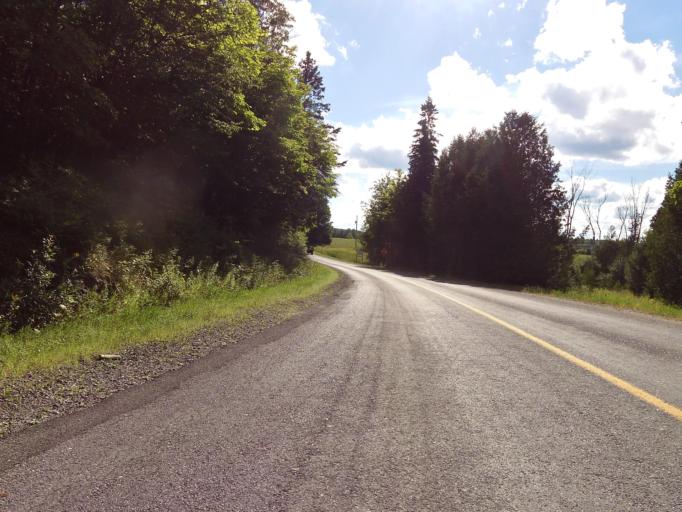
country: CA
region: Ontario
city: Renfrew
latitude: 45.0666
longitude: -76.6445
